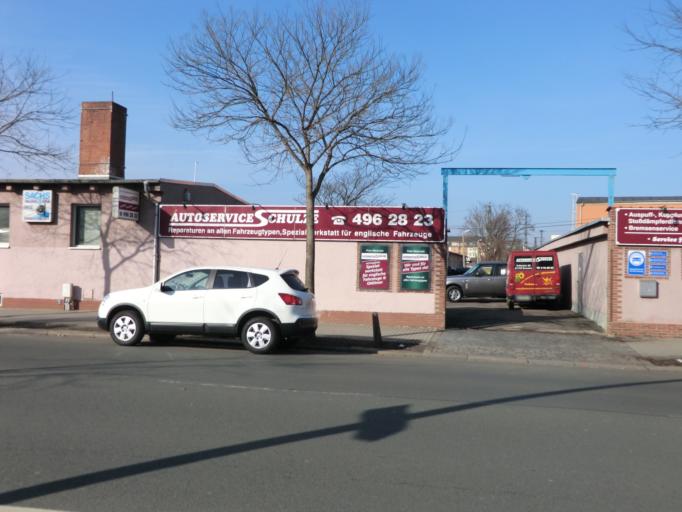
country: DE
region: Saxony
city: Dresden
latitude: 51.0521
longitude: 13.7132
